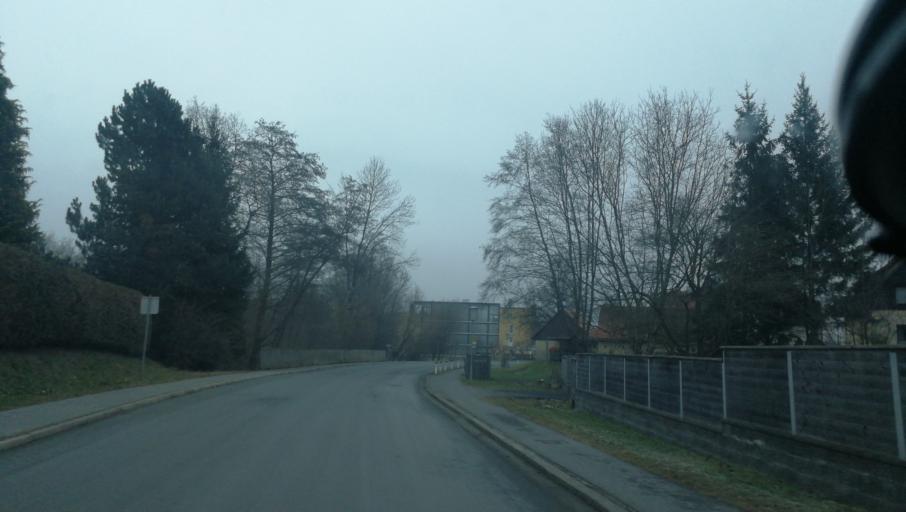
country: AT
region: Styria
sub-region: Politischer Bezirk Deutschlandsberg
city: Stainz
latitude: 46.8931
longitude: 15.2554
